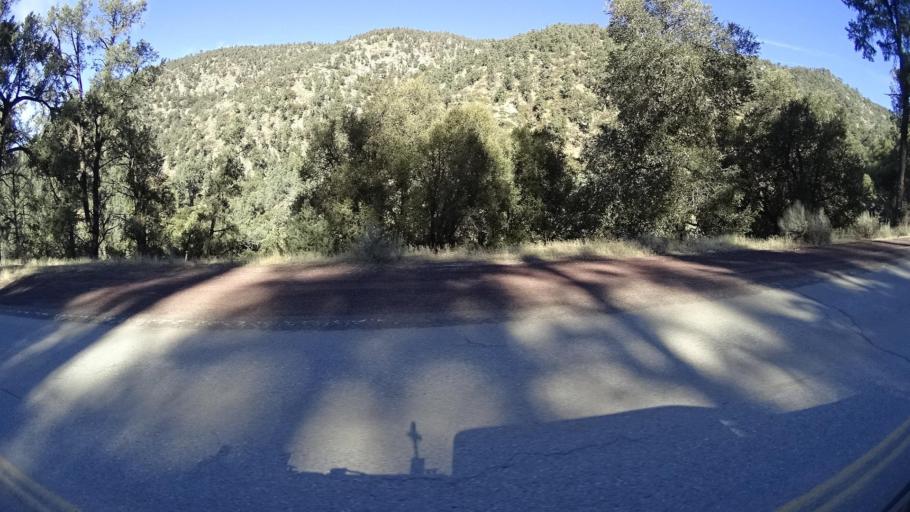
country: US
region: California
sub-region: Kern County
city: Pine Mountain Club
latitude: 34.8505
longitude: -119.1072
